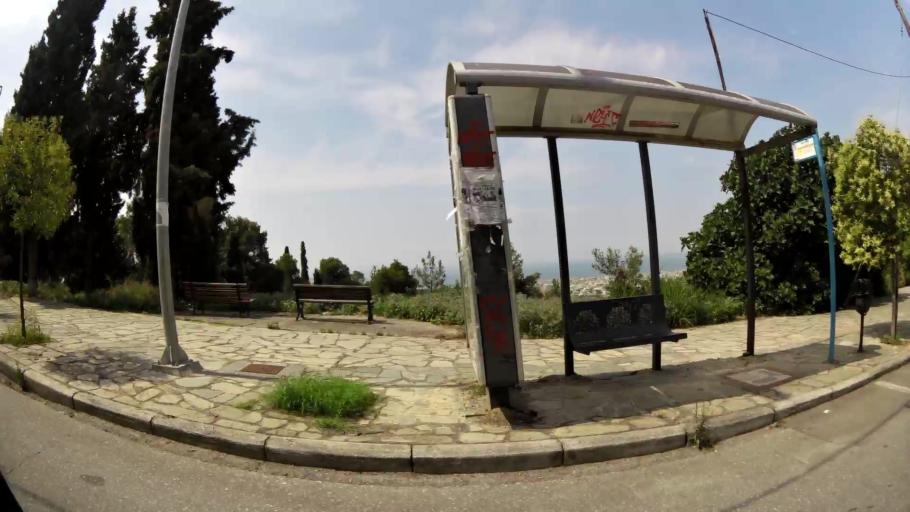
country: GR
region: Central Macedonia
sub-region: Nomos Thessalonikis
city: Agios Pavlos
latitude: 40.6379
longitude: 22.9637
